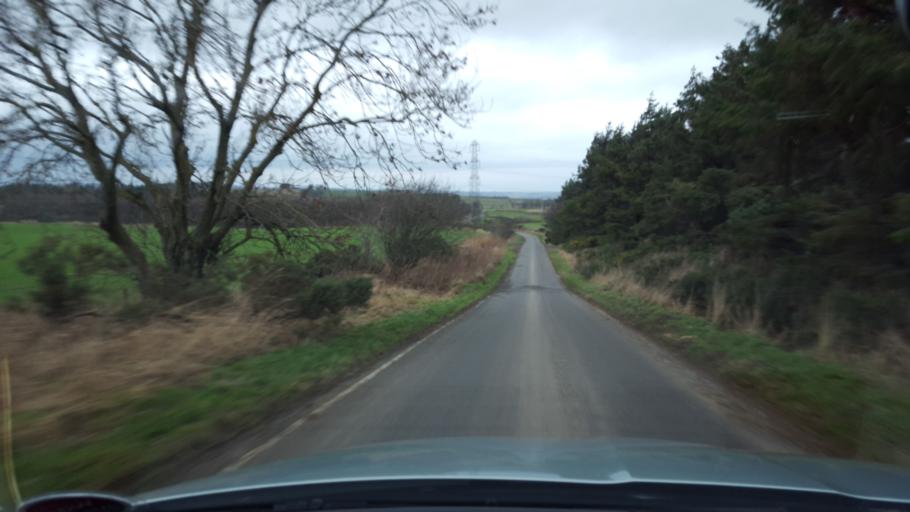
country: GB
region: Scotland
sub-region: West Lothian
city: Kirknewton
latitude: 55.8682
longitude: -3.4341
